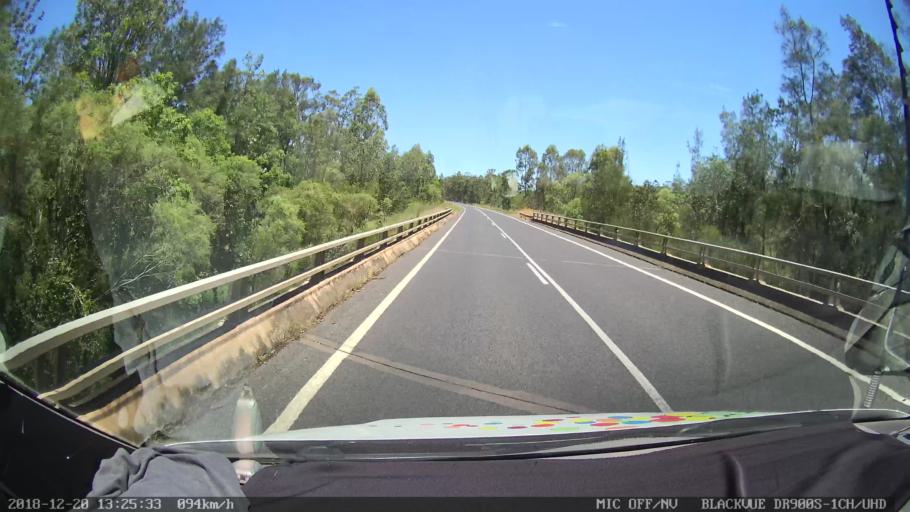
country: AU
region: New South Wales
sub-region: Richmond Valley
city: Casino
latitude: -29.1327
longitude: 152.9961
